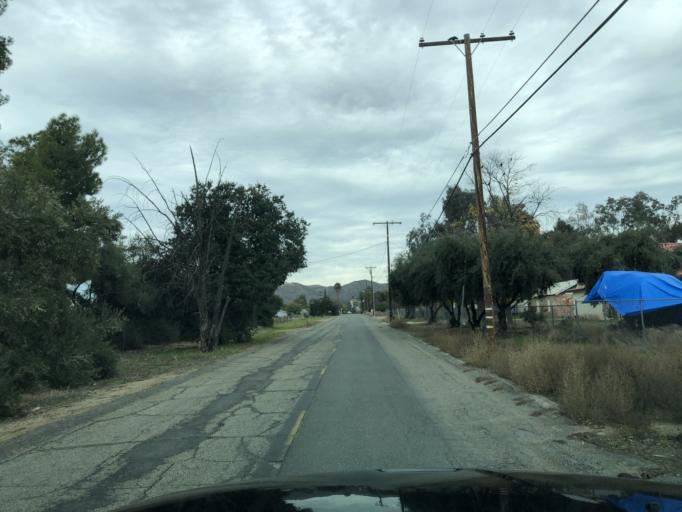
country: US
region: California
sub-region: Riverside County
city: Wildomar
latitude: 33.6170
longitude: -117.2712
